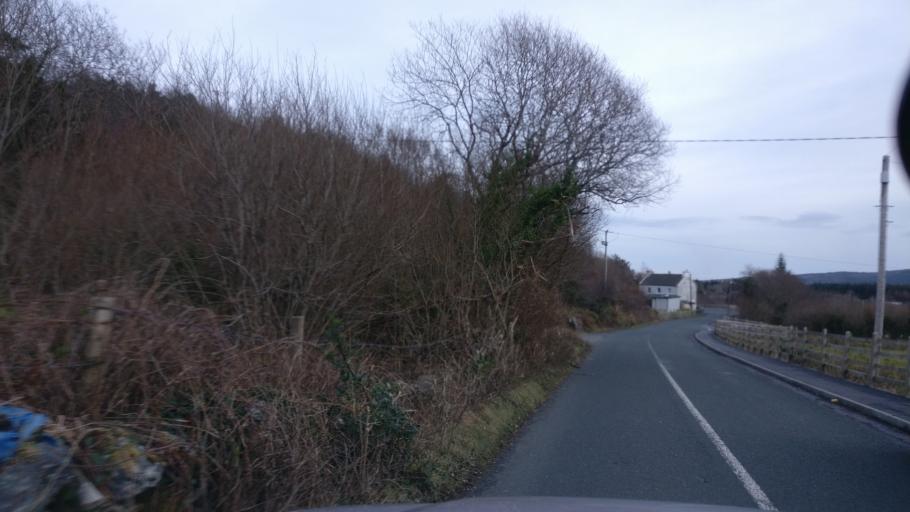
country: IE
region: Connaught
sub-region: County Galway
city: Oughterard
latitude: 53.5196
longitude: -9.4552
